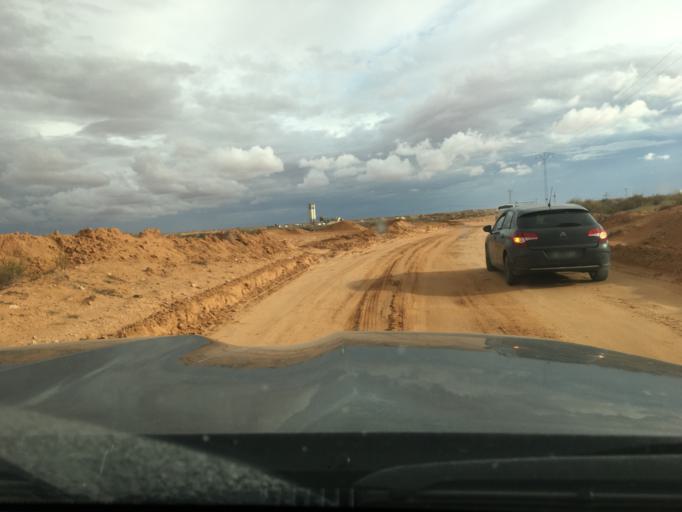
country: TN
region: Madanin
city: Medenine
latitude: 33.2706
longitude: 10.5677
